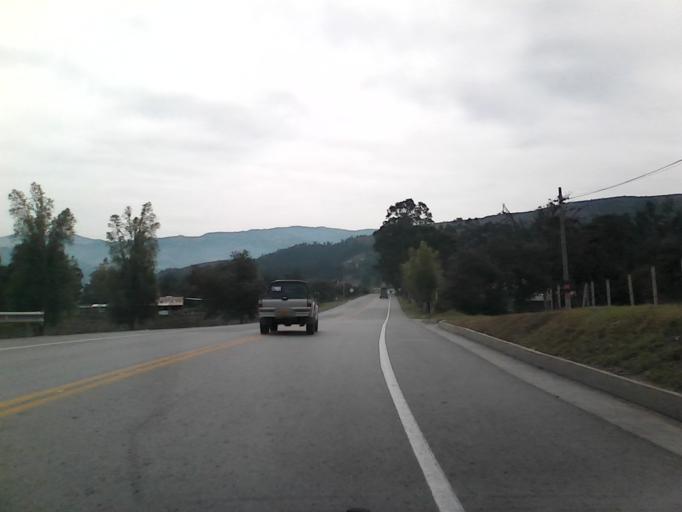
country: CO
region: Boyaca
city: Tibasosa
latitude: 5.7369
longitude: -72.9686
